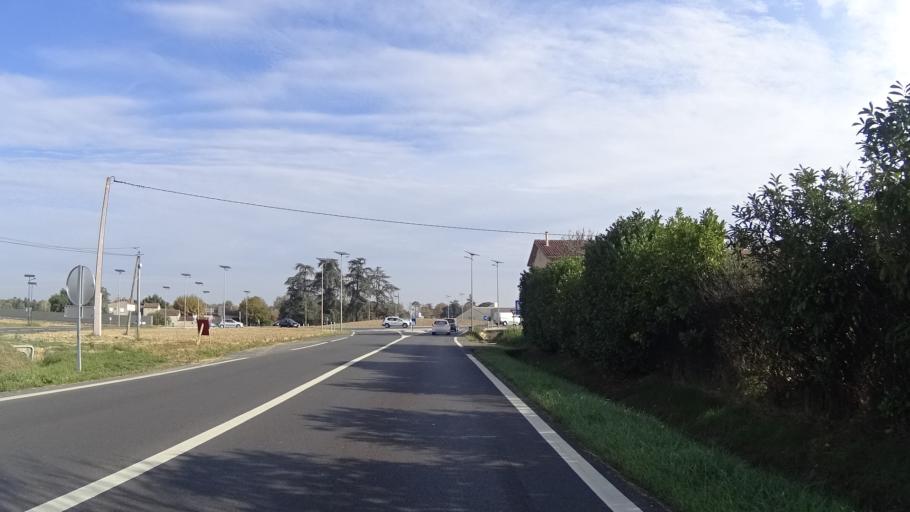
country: FR
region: Aquitaine
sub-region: Departement du Lot-et-Garonne
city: Roquefort
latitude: 44.1812
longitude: 0.5705
